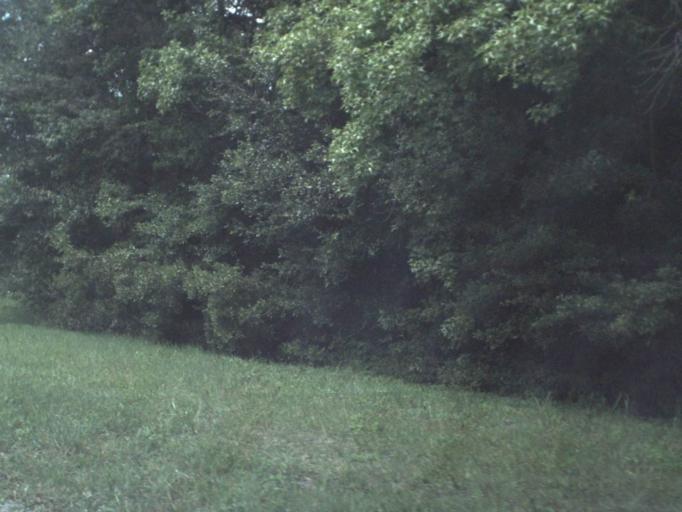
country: US
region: Florida
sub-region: Bradford County
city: Starke
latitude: 30.0393
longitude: -82.0627
